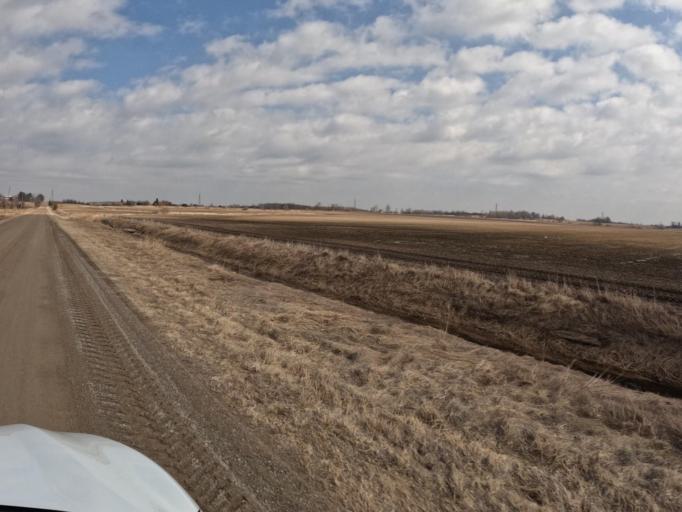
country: CA
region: Ontario
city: Orangeville
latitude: 43.9284
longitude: -80.2411
